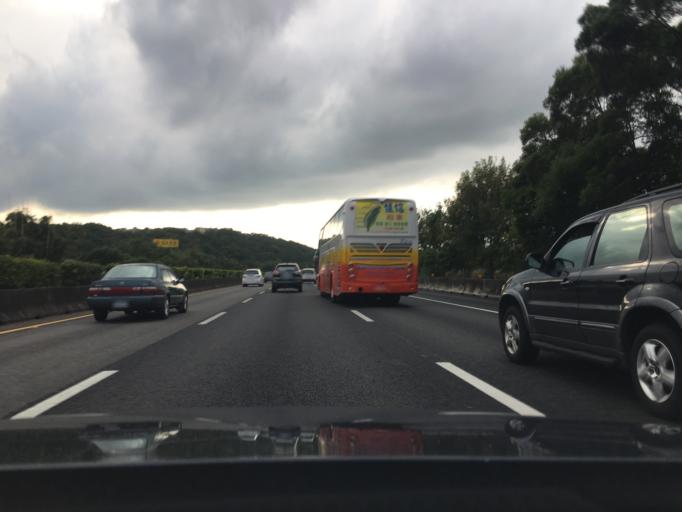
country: TW
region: Taiwan
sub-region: Hsinchu
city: Zhubei
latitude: 24.8933
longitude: 121.1226
